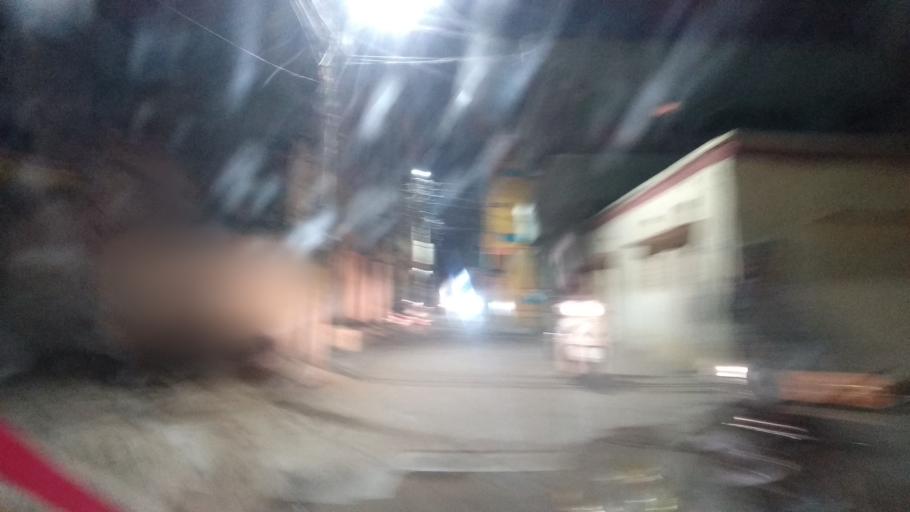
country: IN
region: Telangana
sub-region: Rangareddi
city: Kukatpalli
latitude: 17.4557
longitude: 78.4135
